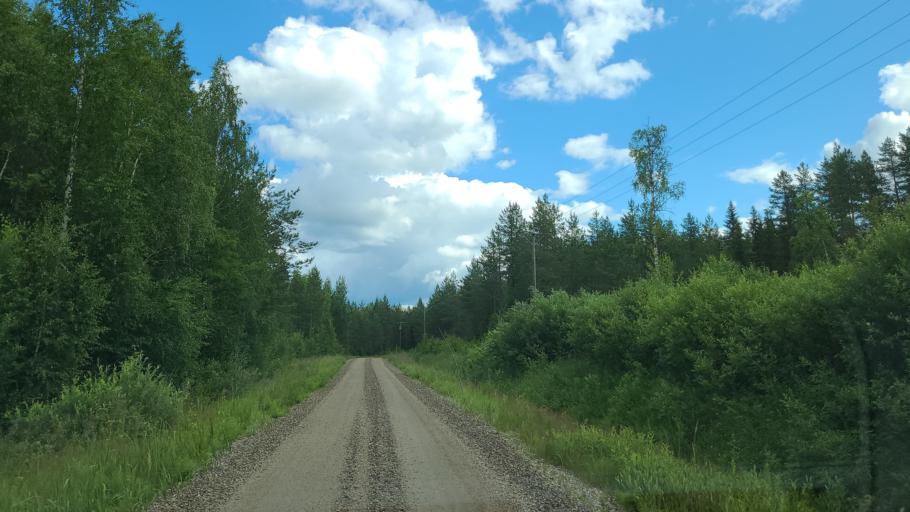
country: FI
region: Northern Savo
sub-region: Koillis-Savo
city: Kaavi
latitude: 63.0408
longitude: 28.8086
